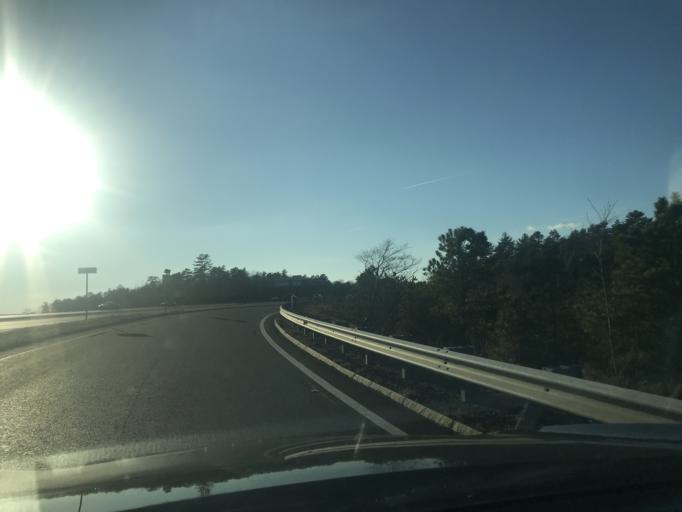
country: US
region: Massachusetts
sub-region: Plymouth County
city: North Plymouth
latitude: 41.9589
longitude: -70.7150
